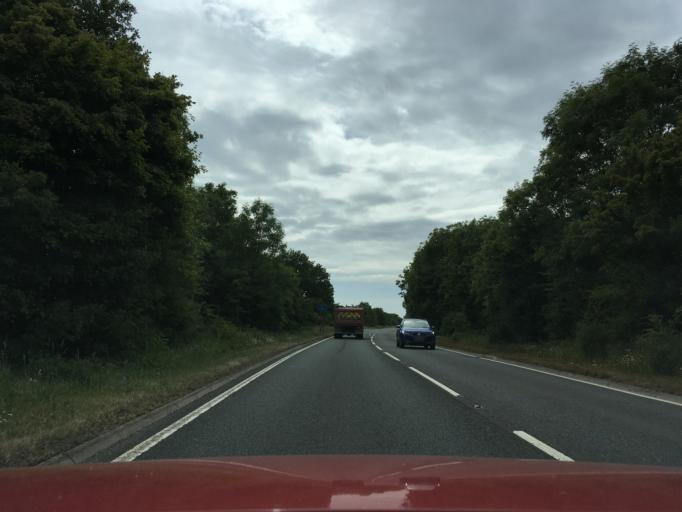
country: GB
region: England
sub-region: South Gloucestershire
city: Severn Beach
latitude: 51.5910
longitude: -2.6266
